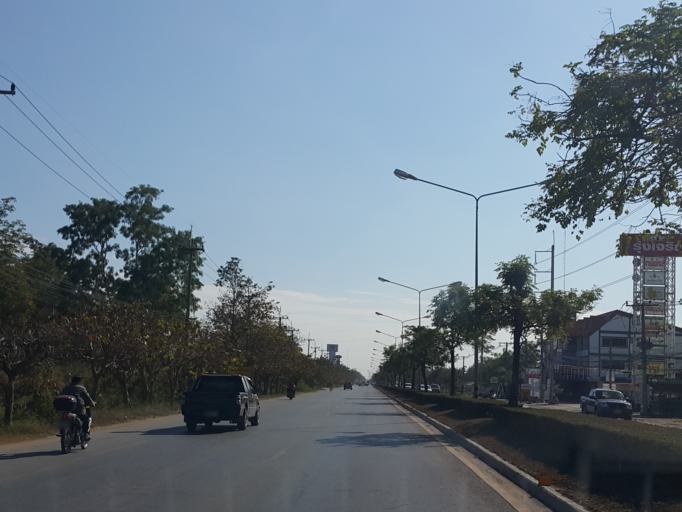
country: TH
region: Chiang Mai
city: San Sai
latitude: 18.8628
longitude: 99.0149
